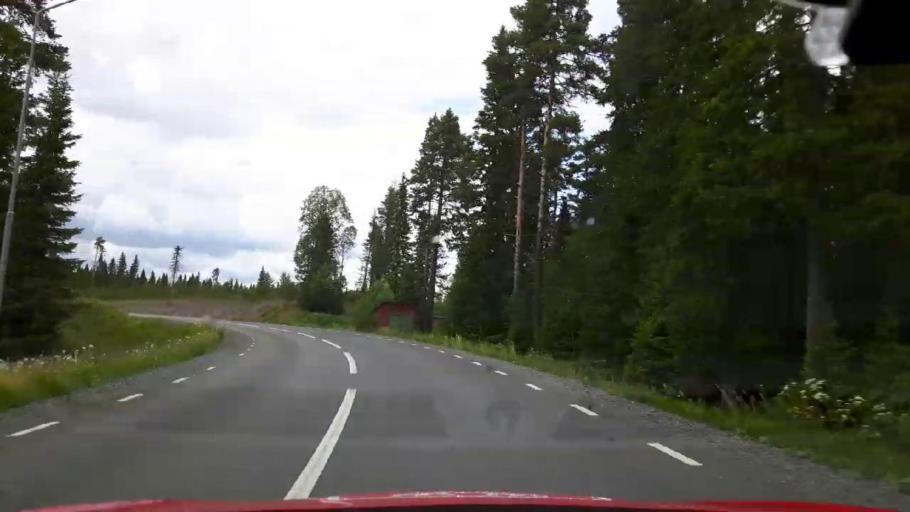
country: SE
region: Jaemtland
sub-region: Krokoms Kommun
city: Krokom
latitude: 63.5716
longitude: 14.2829
